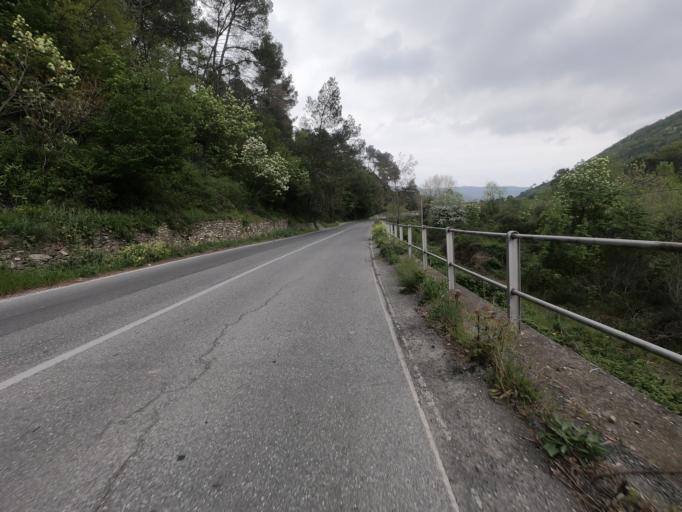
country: IT
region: Liguria
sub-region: Provincia di Savona
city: Garlenda
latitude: 44.0035
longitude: 8.0968
